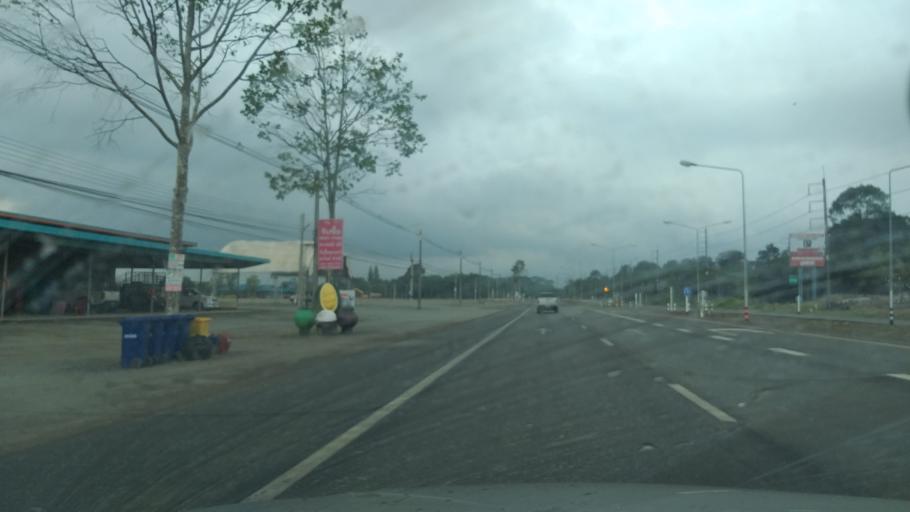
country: TH
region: Chanthaburi
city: Khlung
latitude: 12.4416
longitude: 102.2992
